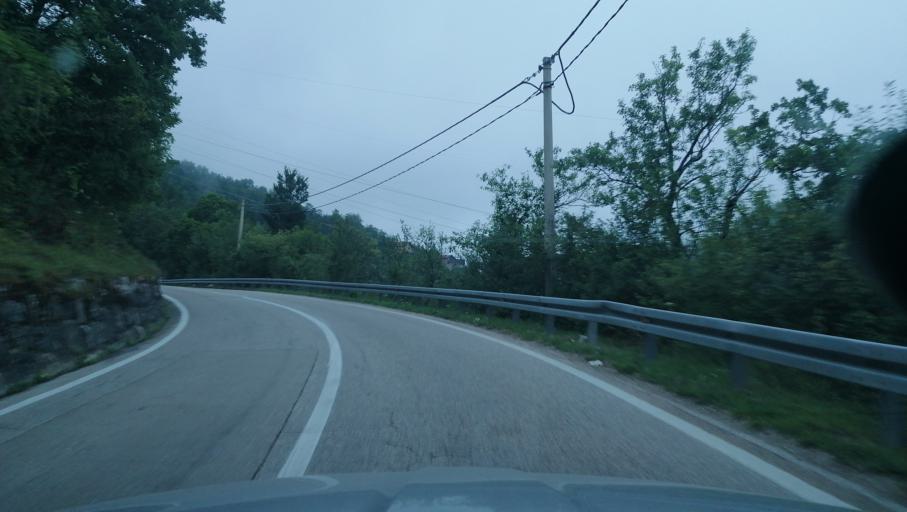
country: BA
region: Federation of Bosnia and Herzegovina
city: Jablanica
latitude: 43.7043
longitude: 17.7177
